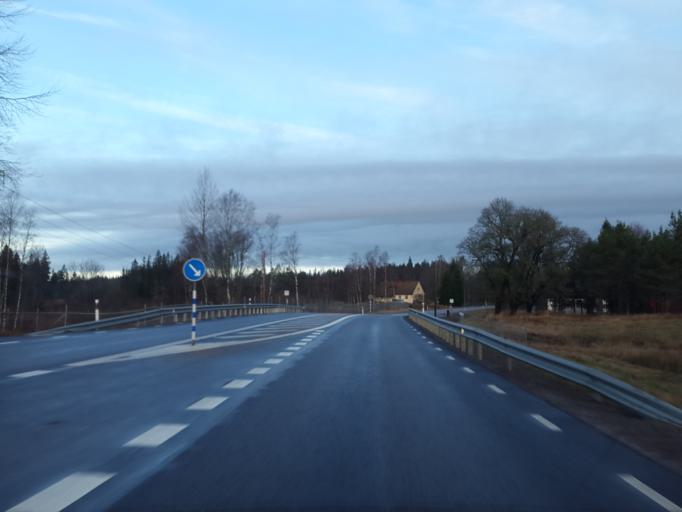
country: SE
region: Vaestra Goetaland
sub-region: Boras Kommun
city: Sandared
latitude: 57.7792
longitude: 12.7835
